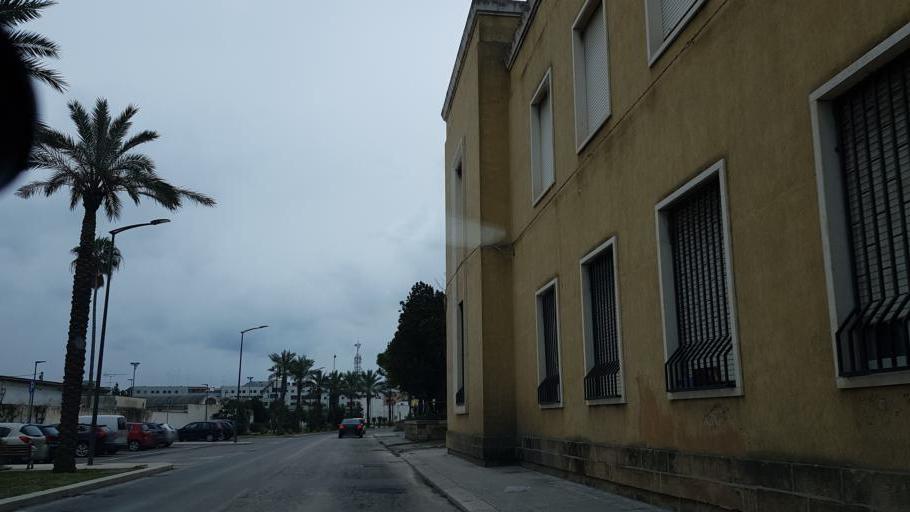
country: IT
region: Apulia
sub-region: Provincia di Brindisi
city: Brindisi
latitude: 40.6340
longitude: 17.9478
